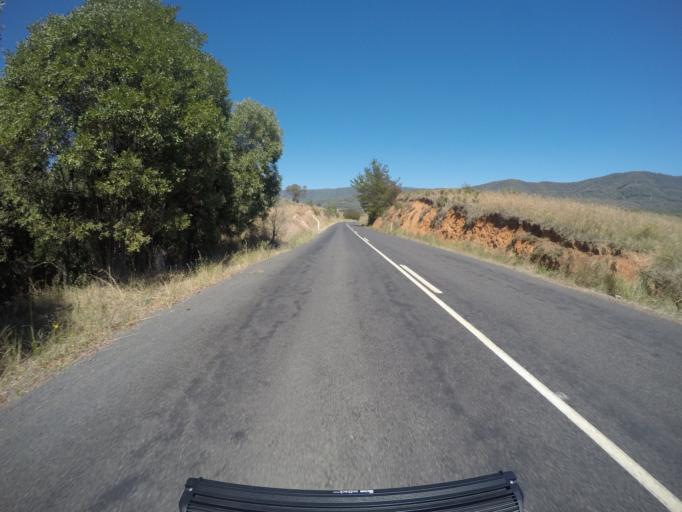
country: AU
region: New South Wales
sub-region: Tumut Shire
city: Tumut
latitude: -35.5859
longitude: 148.2883
